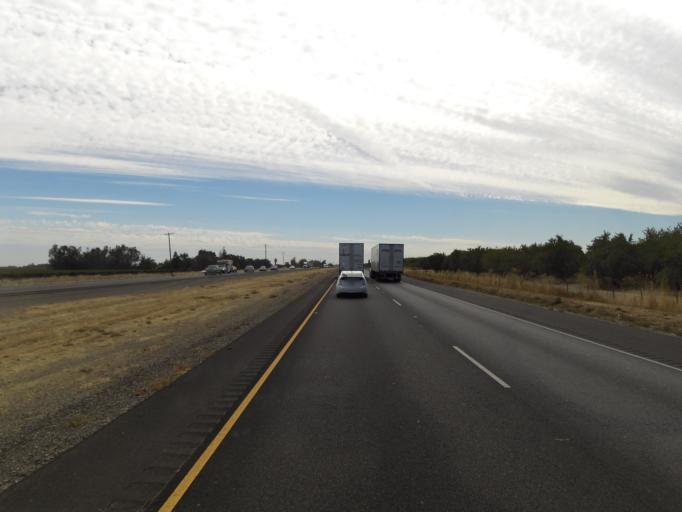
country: US
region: California
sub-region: Colusa County
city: Arbuckle
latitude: 39.0007
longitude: -122.0465
